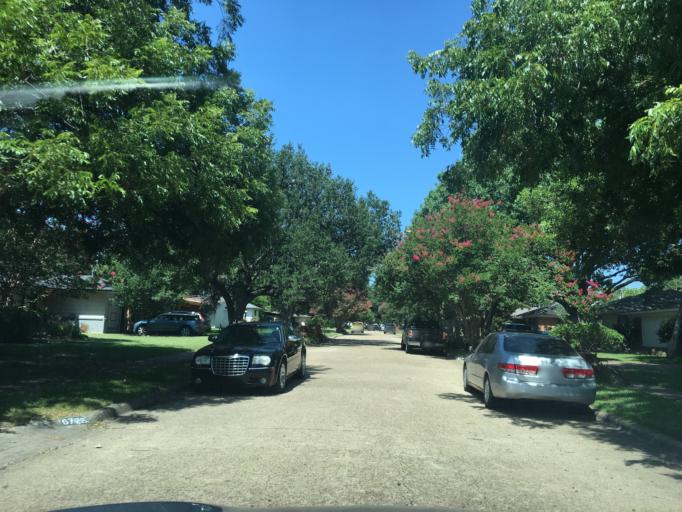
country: US
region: Texas
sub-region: Dallas County
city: Highland Park
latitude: 32.8432
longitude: -96.7435
